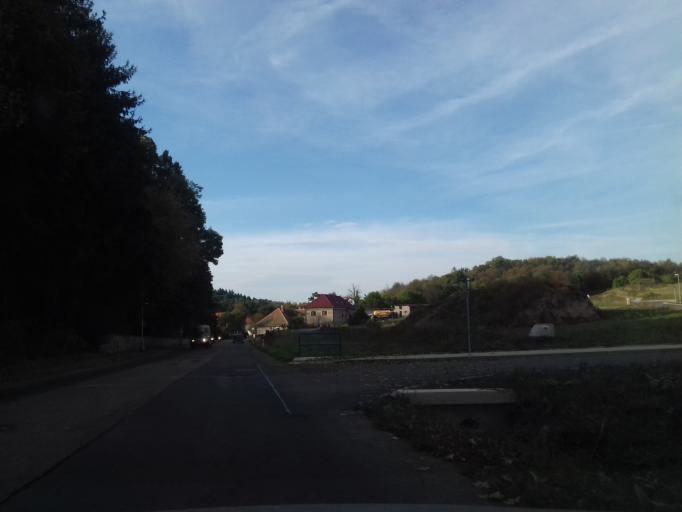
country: CZ
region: Central Bohemia
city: Neveklov
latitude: 49.7578
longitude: 14.5287
